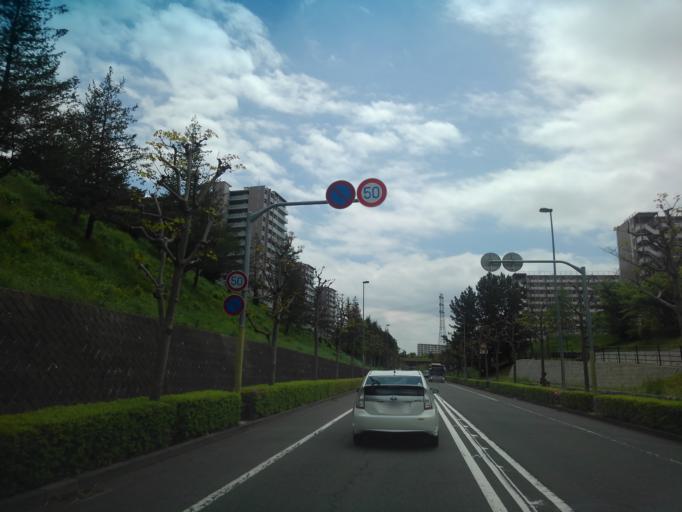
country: JP
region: Tokyo
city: Hino
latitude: 35.6276
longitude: 139.4492
